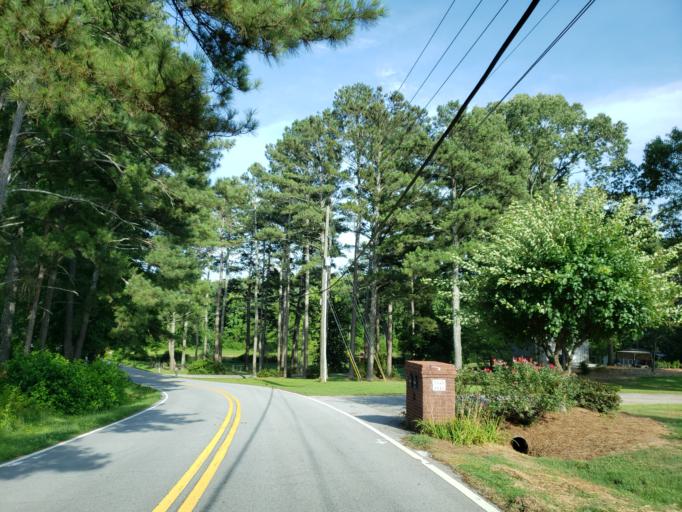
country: US
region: Georgia
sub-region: Paulding County
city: Hiram
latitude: 33.9125
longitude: -84.7157
